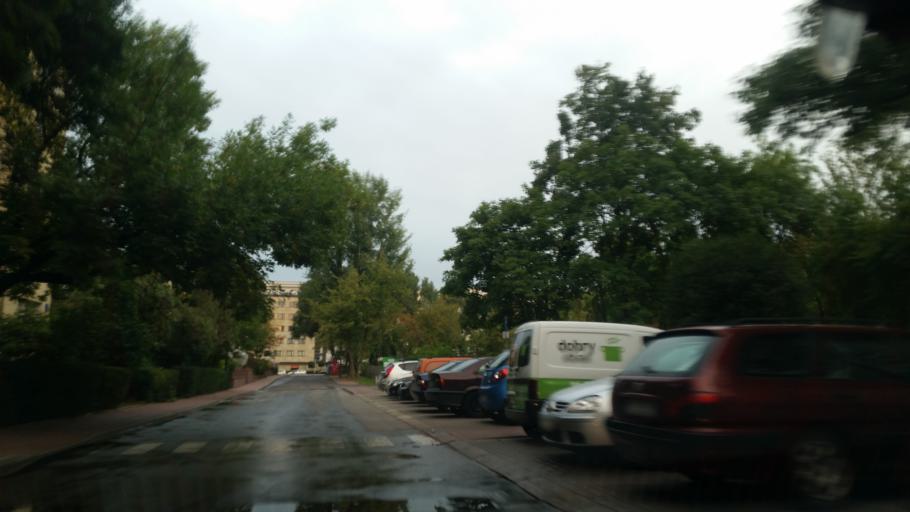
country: PL
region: Masovian Voivodeship
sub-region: Warszawa
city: Mokotow
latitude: 52.1812
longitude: 21.0521
